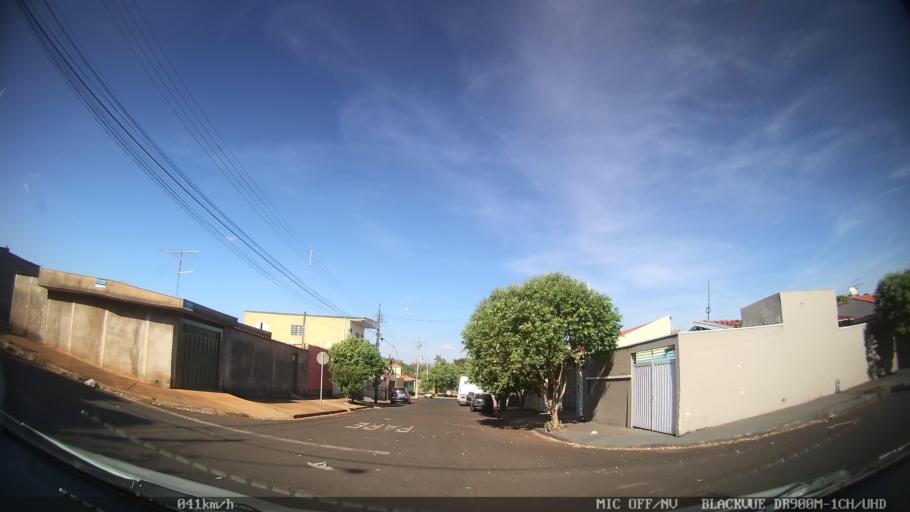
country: BR
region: Sao Paulo
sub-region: Ribeirao Preto
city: Ribeirao Preto
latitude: -21.1833
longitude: -47.7643
